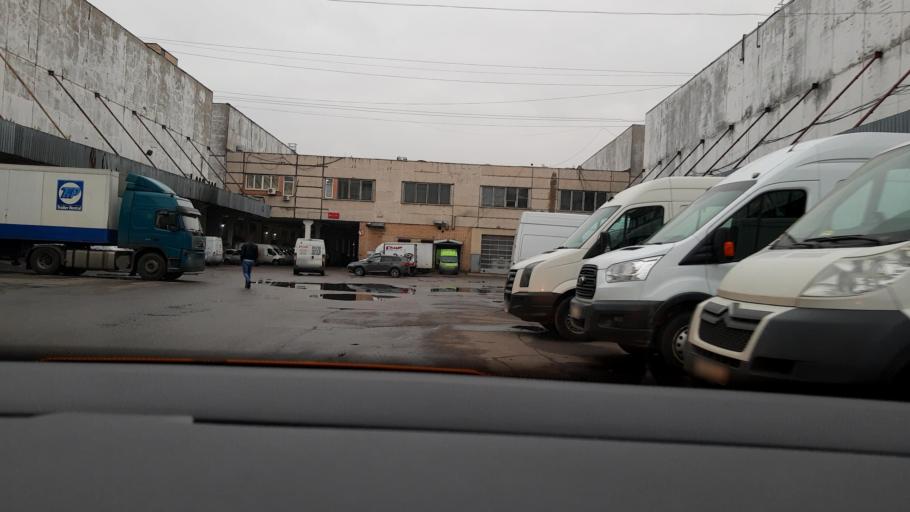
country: RU
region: Moskovskaya
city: Presnenskiy
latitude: 55.7726
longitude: 37.5297
